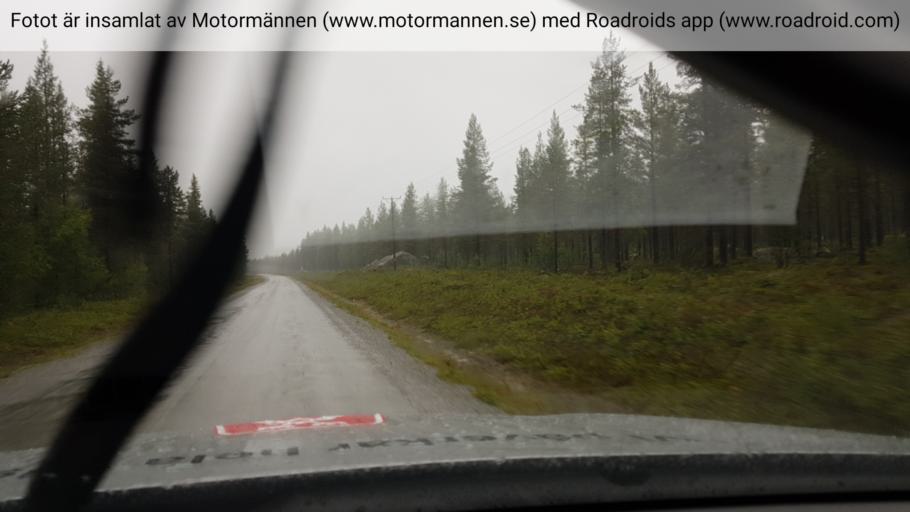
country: SE
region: Norrbotten
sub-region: Jokkmokks Kommun
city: Jokkmokk
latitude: 66.6172
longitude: 18.9395
